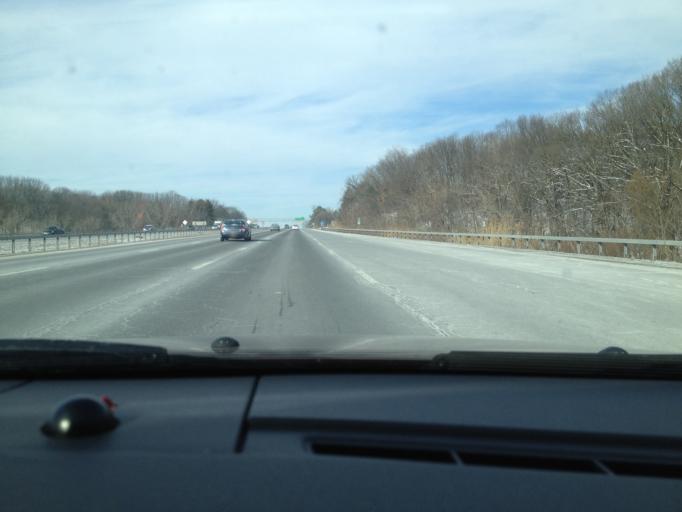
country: US
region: New York
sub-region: Albany County
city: Albany
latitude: 42.6716
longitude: -73.7551
